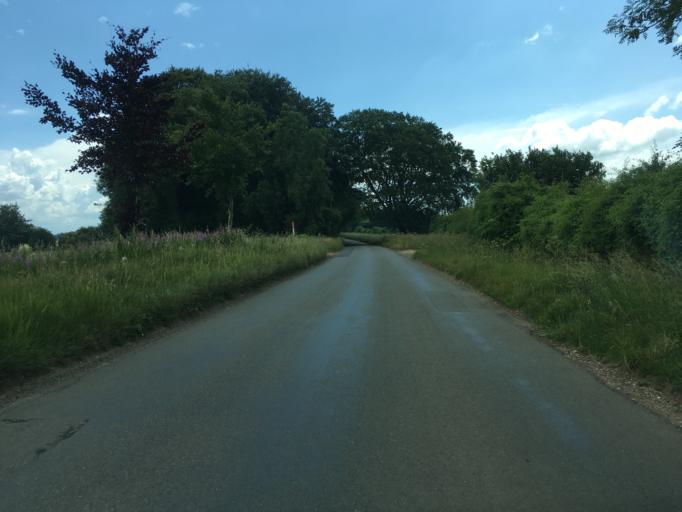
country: GB
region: England
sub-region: Gloucestershire
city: Coates
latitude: 51.7318
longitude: -2.0609
